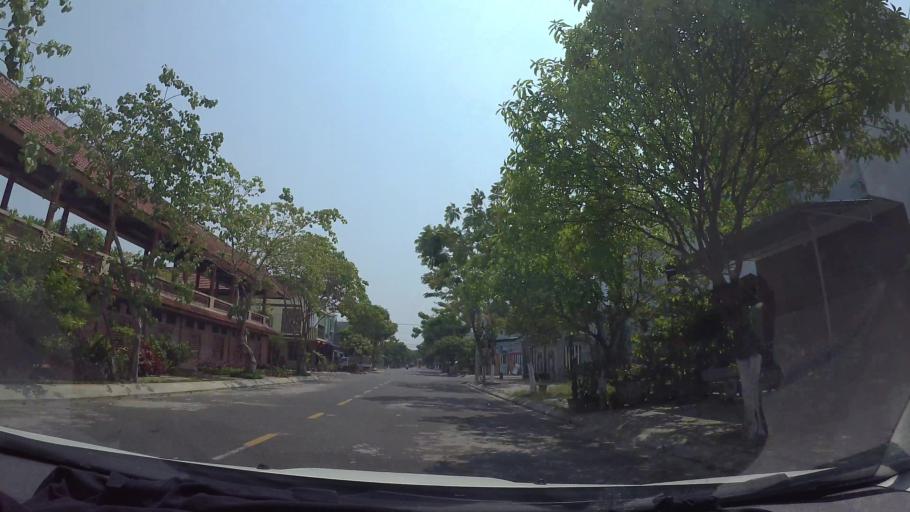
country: VN
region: Da Nang
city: Cam Le
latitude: 15.9984
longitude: 108.2047
